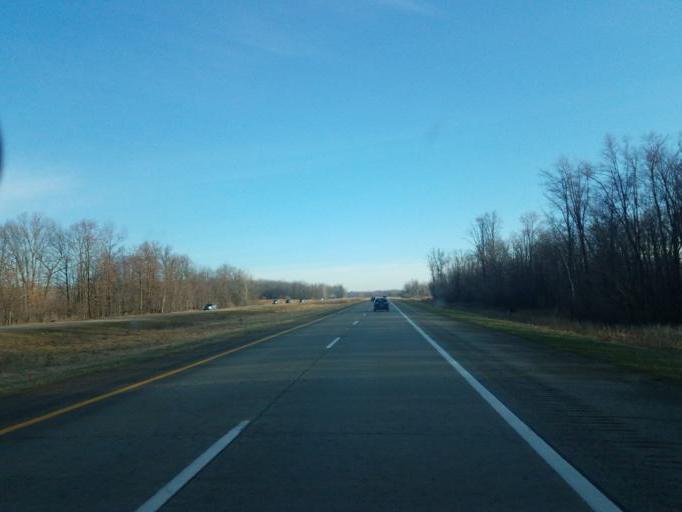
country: US
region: Michigan
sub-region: Clinton County
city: DeWitt
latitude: 42.8718
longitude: -84.5176
